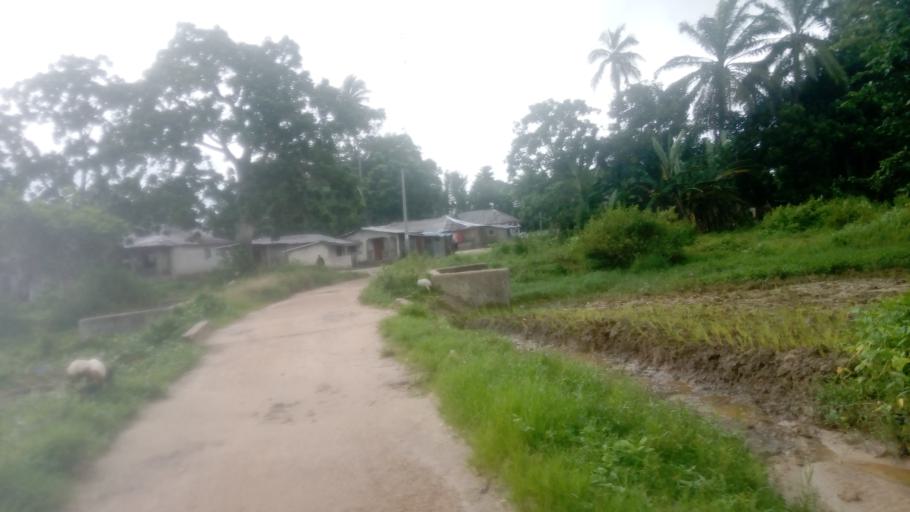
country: SL
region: Northern Province
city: Lunsar
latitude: 8.6842
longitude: -12.5395
